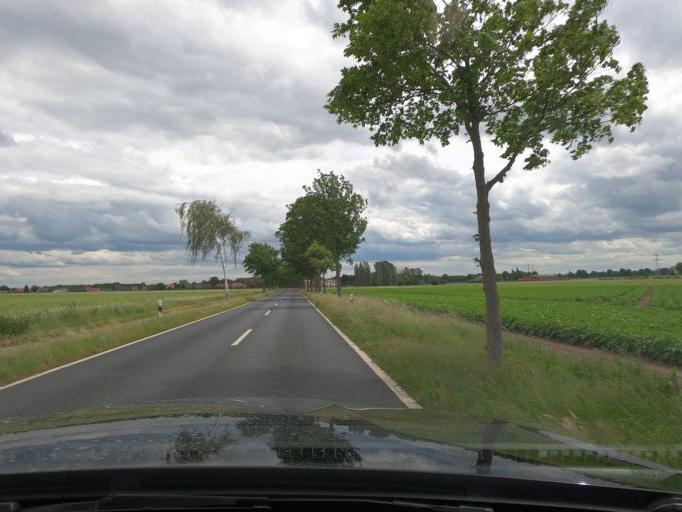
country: DE
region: Lower Saxony
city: Lehrte
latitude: 52.4186
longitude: 9.9666
